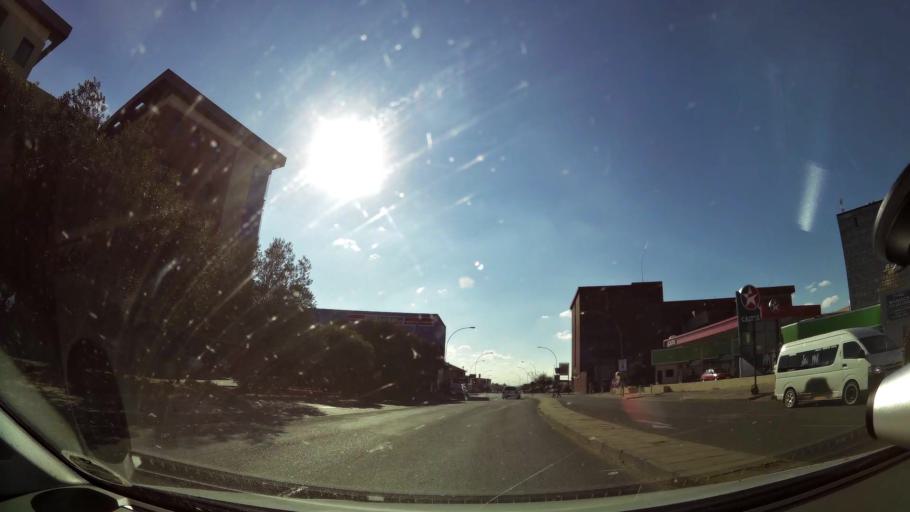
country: ZA
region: Northern Cape
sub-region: Frances Baard District Municipality
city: Kimberley
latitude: -28.7432
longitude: 24.7624
